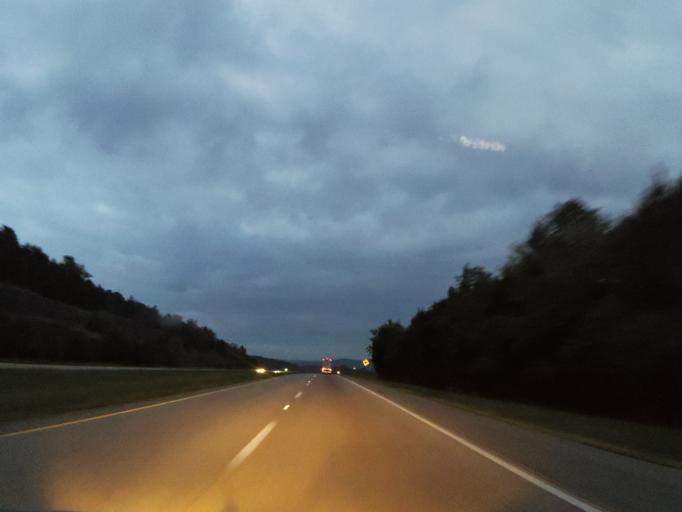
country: US
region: Alabama
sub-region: Madison County
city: New Hope
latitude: 34.6106
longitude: -86.2765
